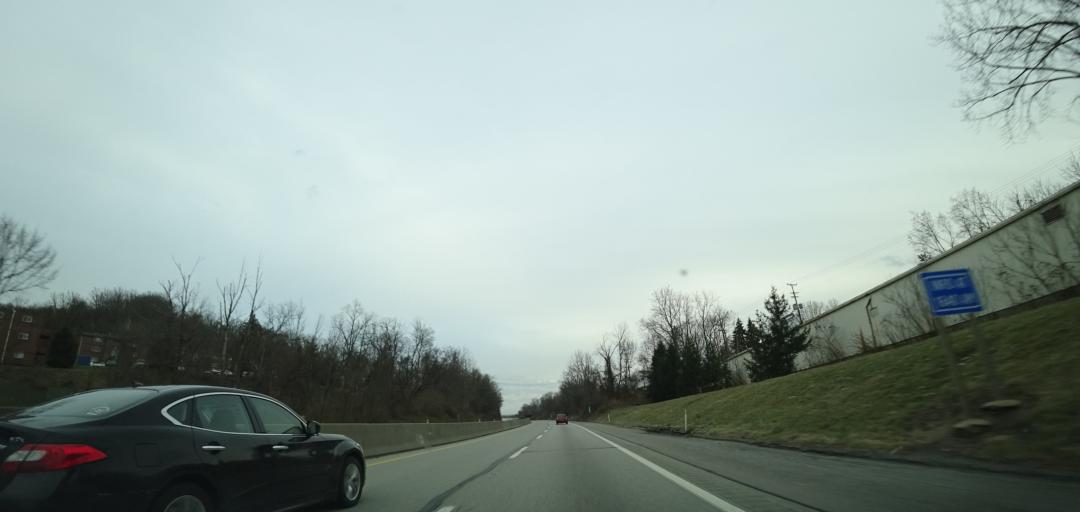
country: US
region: Pennsylvania
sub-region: Allegheny County
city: Plum
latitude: 40.4619
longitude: -79.7606
